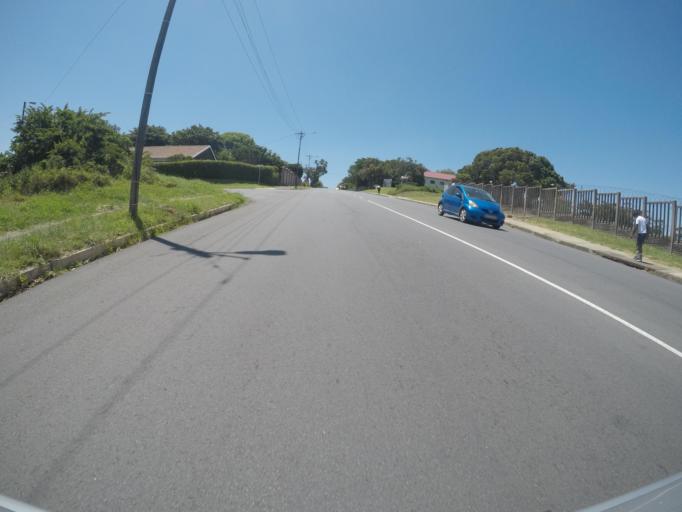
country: ZA
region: Eastern Cape
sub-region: Buffalo City Metropolitan Municipality
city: East London
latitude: -32.9873
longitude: 27.9108
